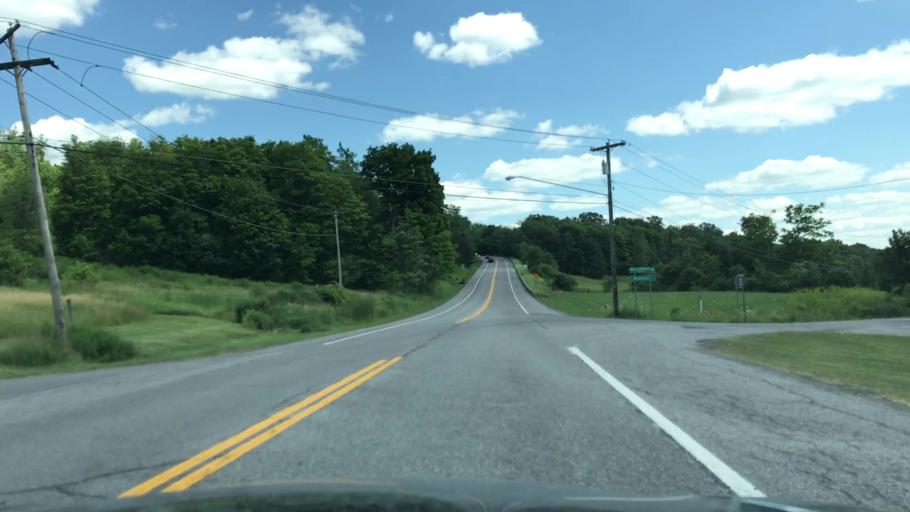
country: US
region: New York
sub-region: Erie County
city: East Aurora
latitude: 42.7665
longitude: -78.5189
